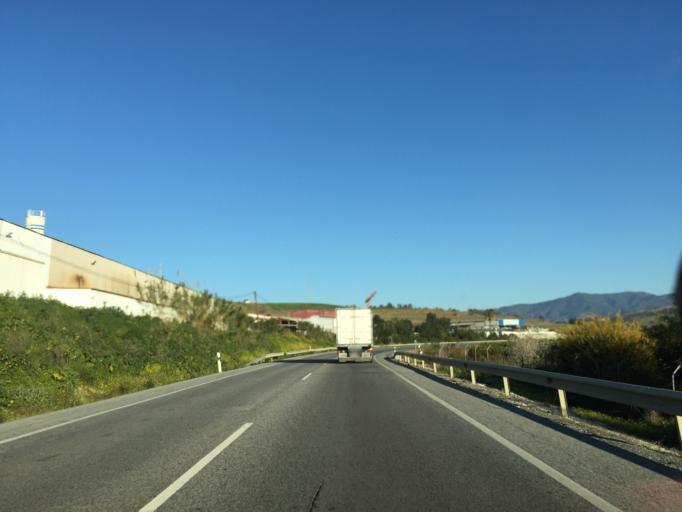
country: ES
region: Andalusia
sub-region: Provincia de Malaga
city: Pizarra
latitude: 36.7583
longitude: -4.7284
